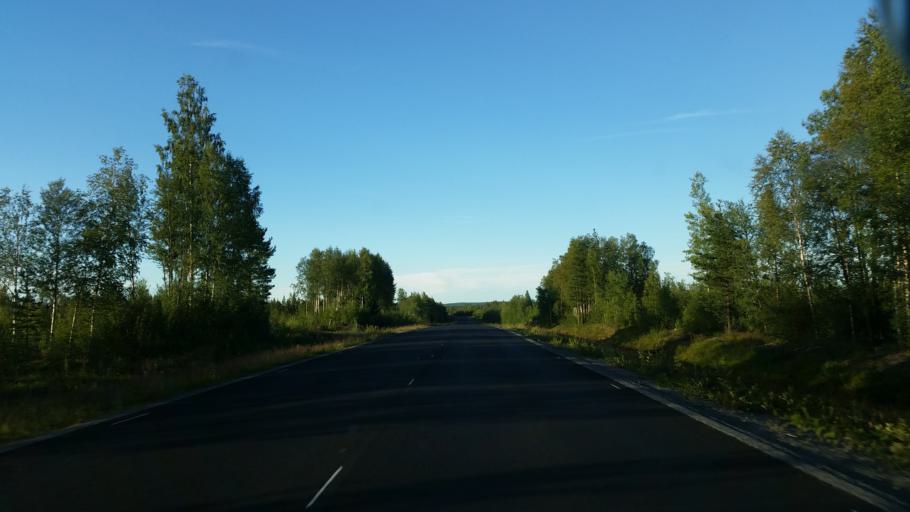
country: SE
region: Vaesterbotten
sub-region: Dorotea Kommun
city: Dorotea
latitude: 64.3225
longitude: 16.6178
